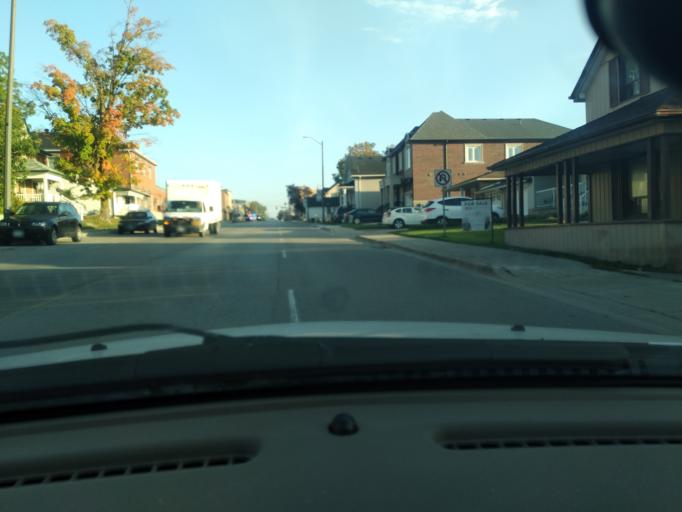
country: CA
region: Ontario
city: Bradford West Gwillimbury
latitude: 44.1126
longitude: -79.5643
